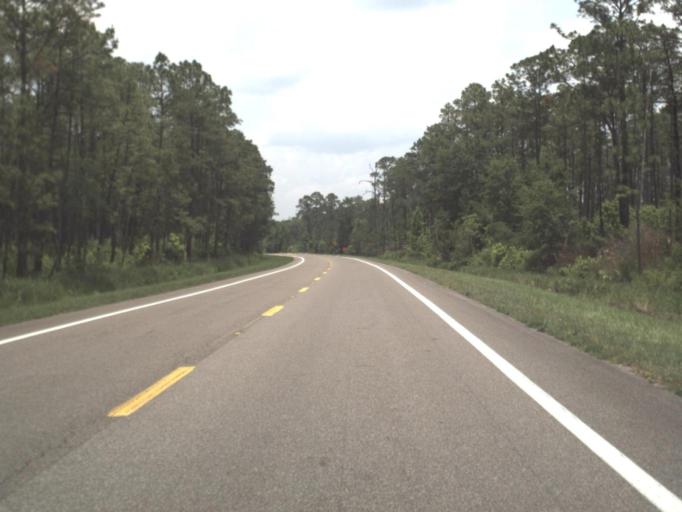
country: US
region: Florida
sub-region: Putnam County
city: Palatka
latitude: 29.4708
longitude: -81.7385
